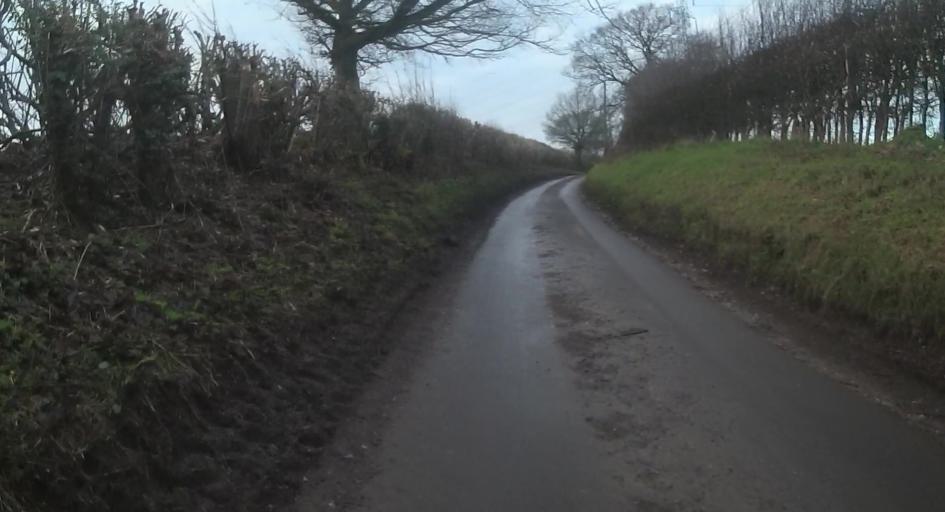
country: GB
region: England
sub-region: Hampshire
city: Kingsclere
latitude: 51.2992
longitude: -1.2304
